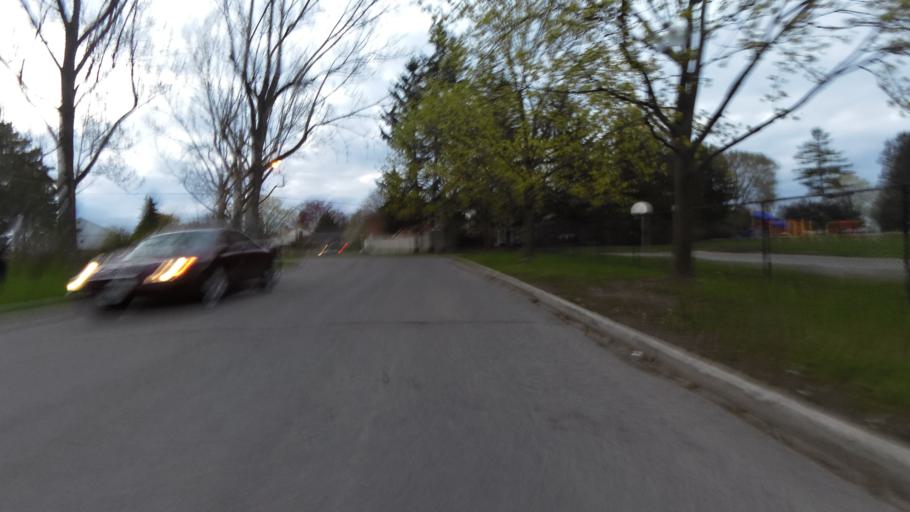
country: CA
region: Ontario
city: Ottawa
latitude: 45.3781
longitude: -75.7229
